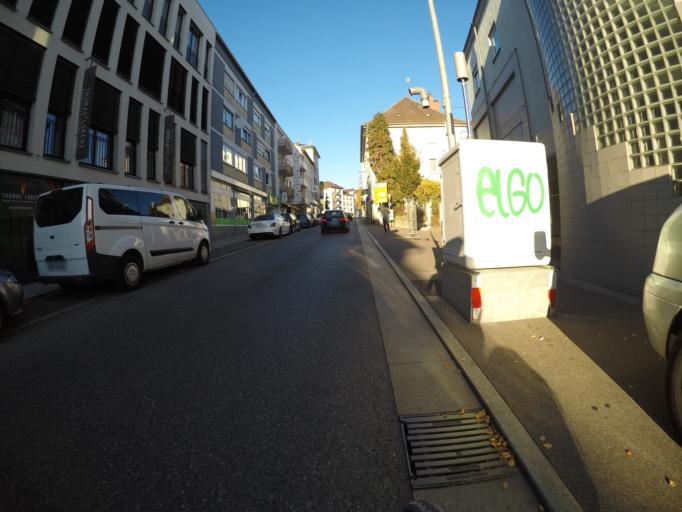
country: DE
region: Baden-Wuerttemberg
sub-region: Regierungsbezirk Stuttgart
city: Boeblingen
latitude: 48.6850
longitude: 9.0145
